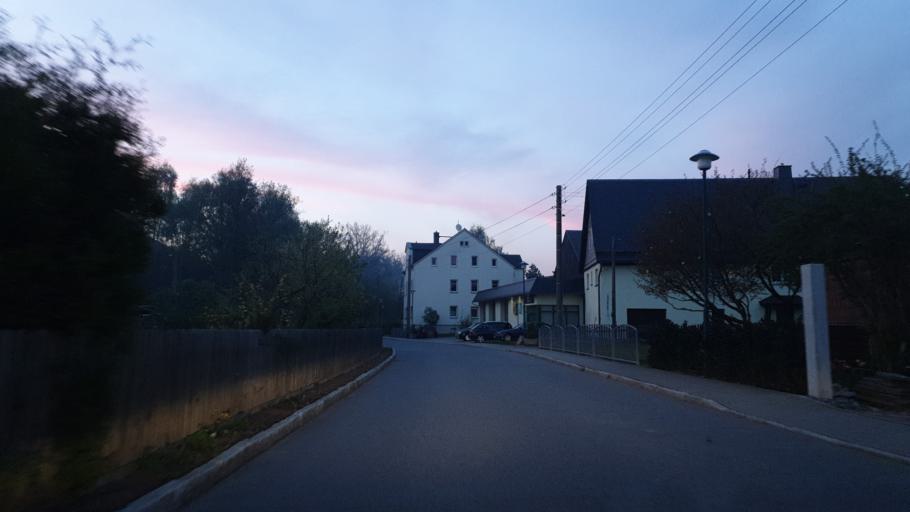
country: DE
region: Saxony
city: Niederdorf
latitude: 50.7227
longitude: 12.7873
